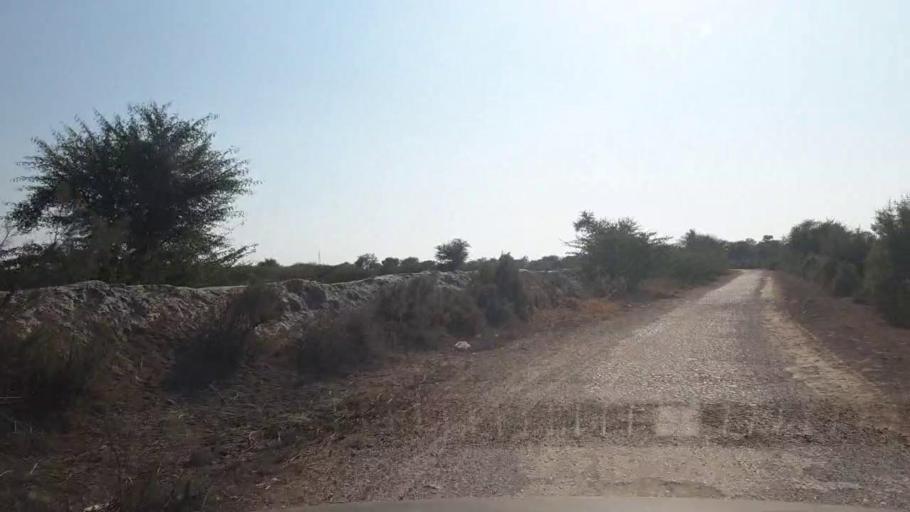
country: PK
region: Sindh
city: Shahpur Chakar
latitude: 26.1501
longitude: 68.6782
